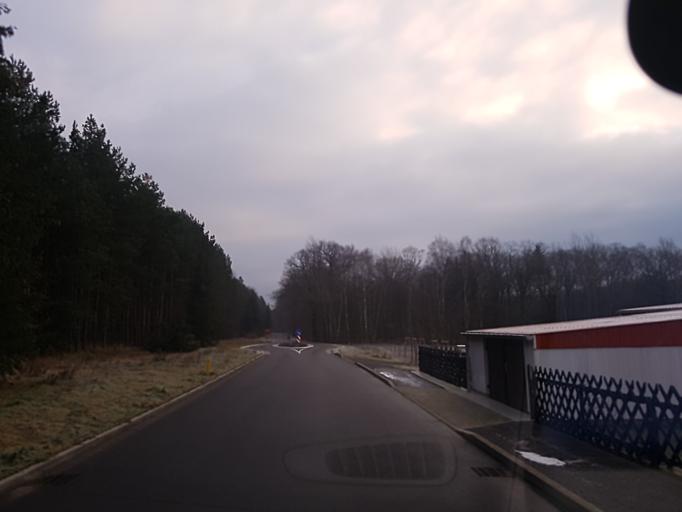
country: DE
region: Brandenburg
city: Crinitz
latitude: 51.7128
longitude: 13.7912
